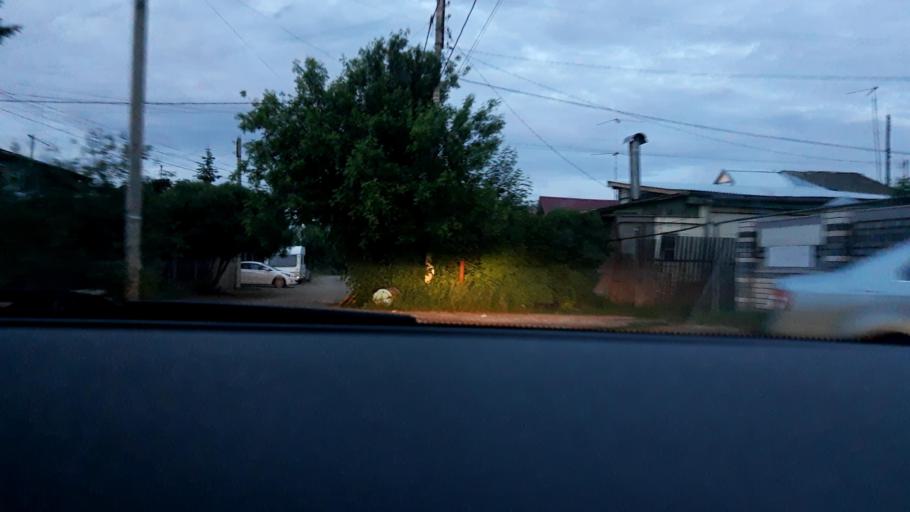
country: RU
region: Nizjnij Novgorod
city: Gorbatovka
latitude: 56.3863
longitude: 43.7694
